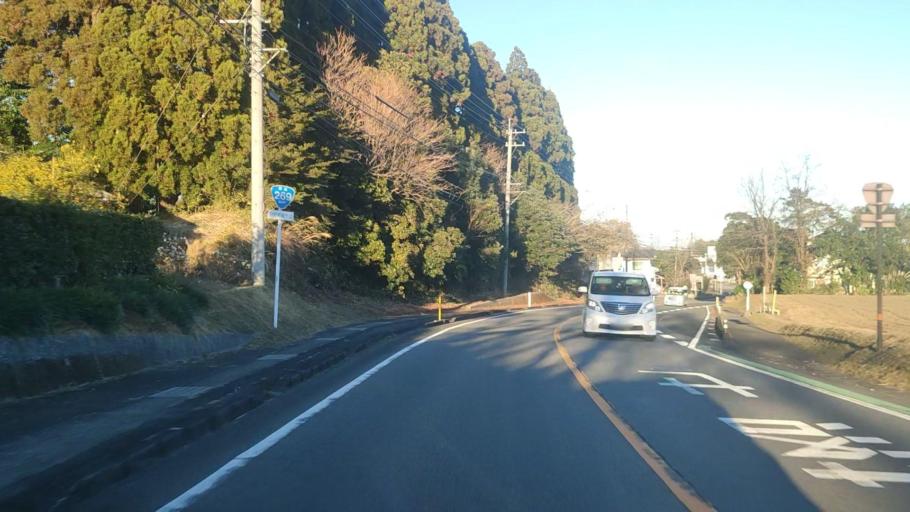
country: JP
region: Miyazaki
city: Miyazaki-shi
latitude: 31.8379
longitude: 131.3333
